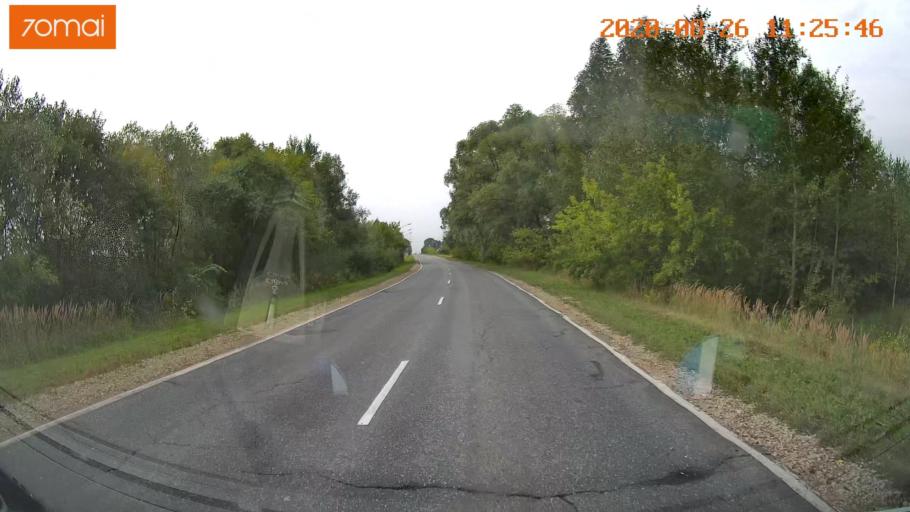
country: RU
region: Rjazan
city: Shilovo
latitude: 54.3392
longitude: 40.9585
